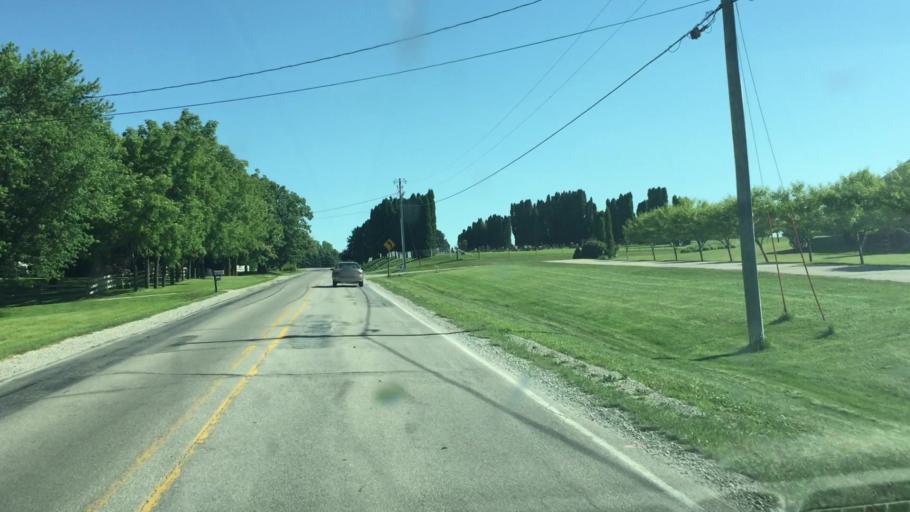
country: US
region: Iowa
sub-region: Linn County
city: Ely
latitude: 41.8455
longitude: -91.6461
